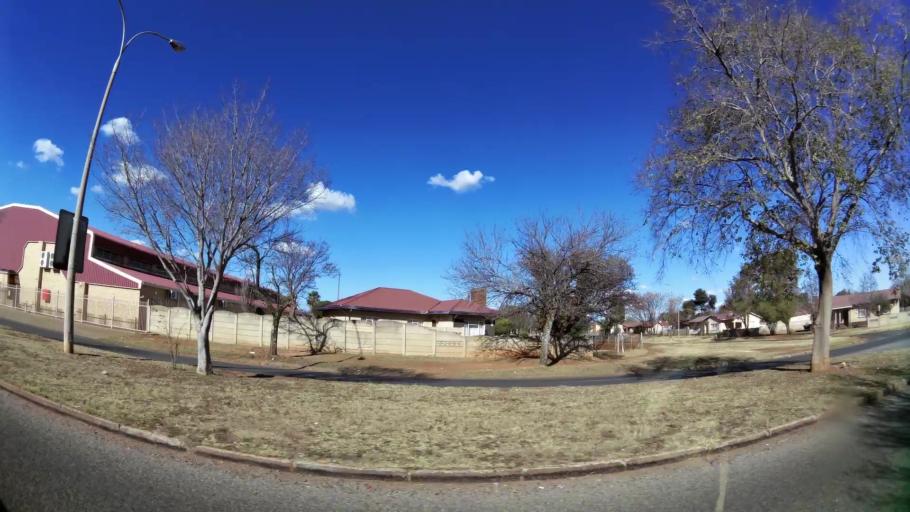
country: ZA
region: Gauteng
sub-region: West Rand District Municipality
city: Carletonville
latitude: -26.3617
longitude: 27.3811
